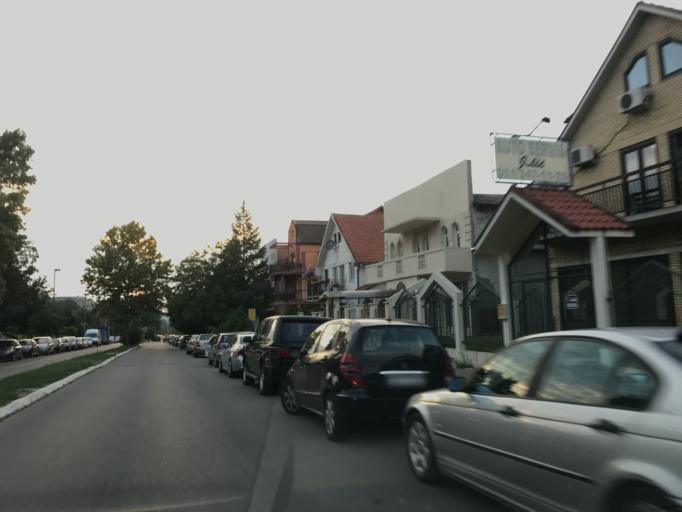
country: RS
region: Central Serbia
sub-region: Belgrade
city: Vozdovac
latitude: 44.7757
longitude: 20.5036
